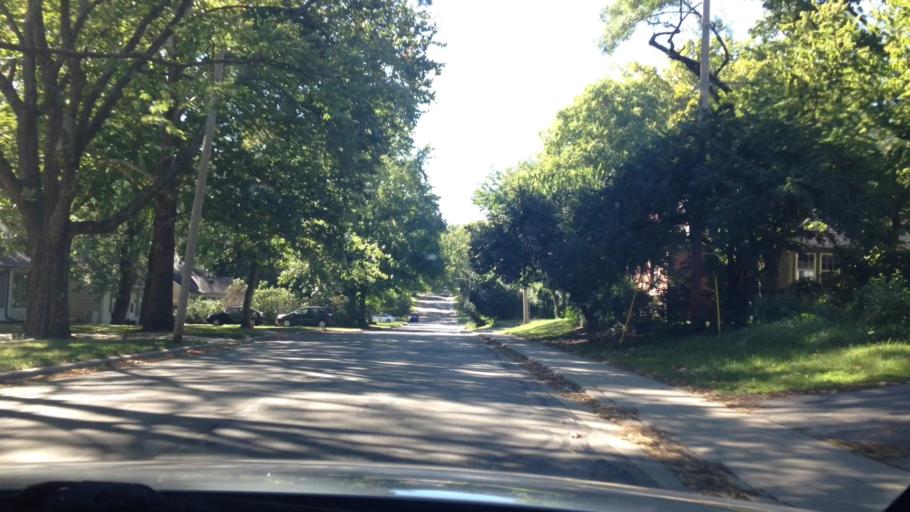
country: US
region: Kansas
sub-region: Johnson County
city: Fairway
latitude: 39.0169
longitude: -94.6350
